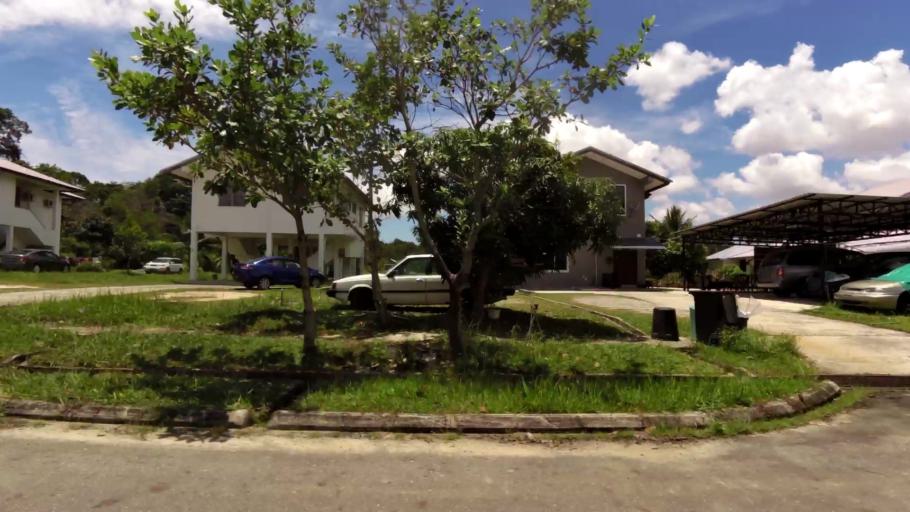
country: BN
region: Brunei and Muara
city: Bandar Seri Begawan
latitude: 4.9666
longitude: 114.9220
